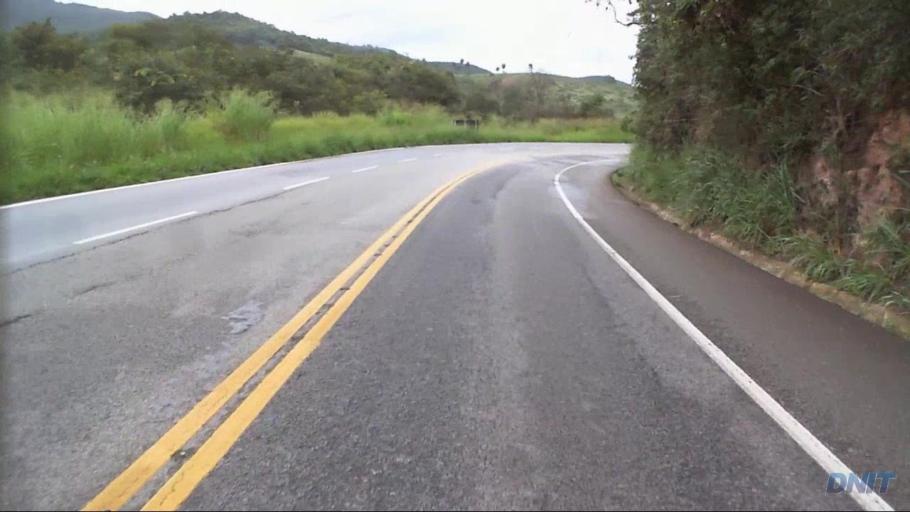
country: BR
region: Minas Gerais
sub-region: Joao Monlevade
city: Joao Monlevade
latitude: -19.8401
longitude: -43.3237
